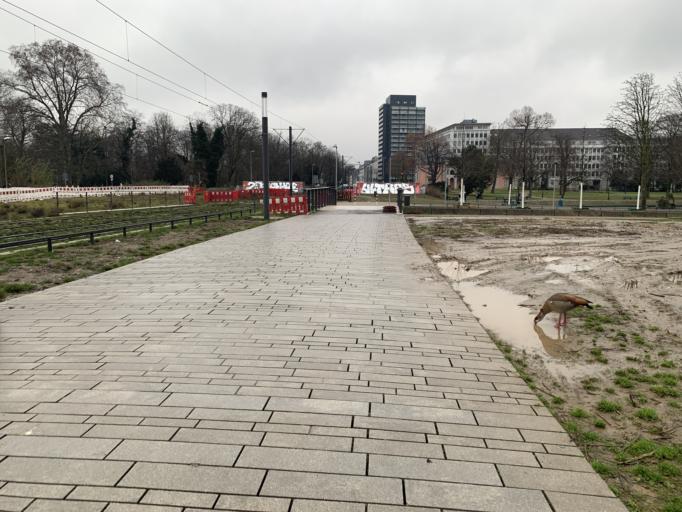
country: DE
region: North Rhine-Westphalia
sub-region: Regierungsbezirk Dusseldorf
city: Dusseldorf
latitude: 51.2283
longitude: 6.7816
